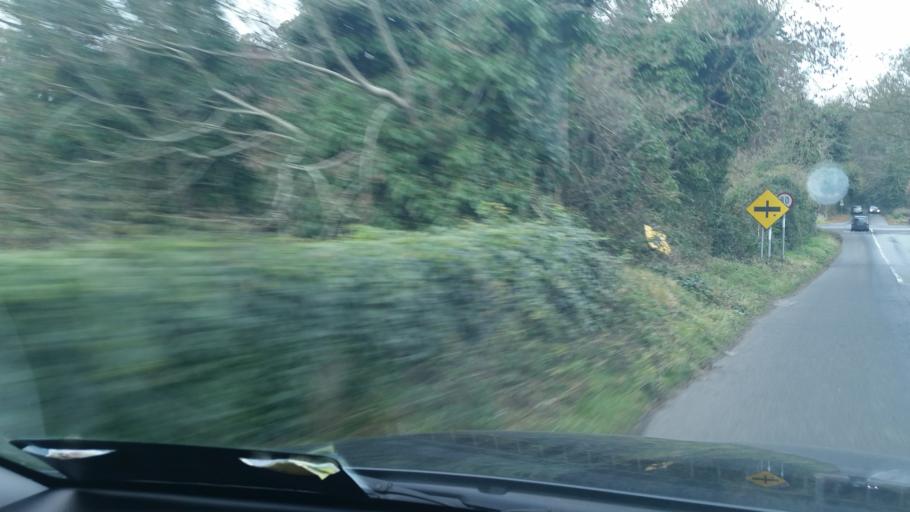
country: IE
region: Leinster
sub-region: Lu
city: Tullyallen
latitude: 53.7253
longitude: -6.4169
